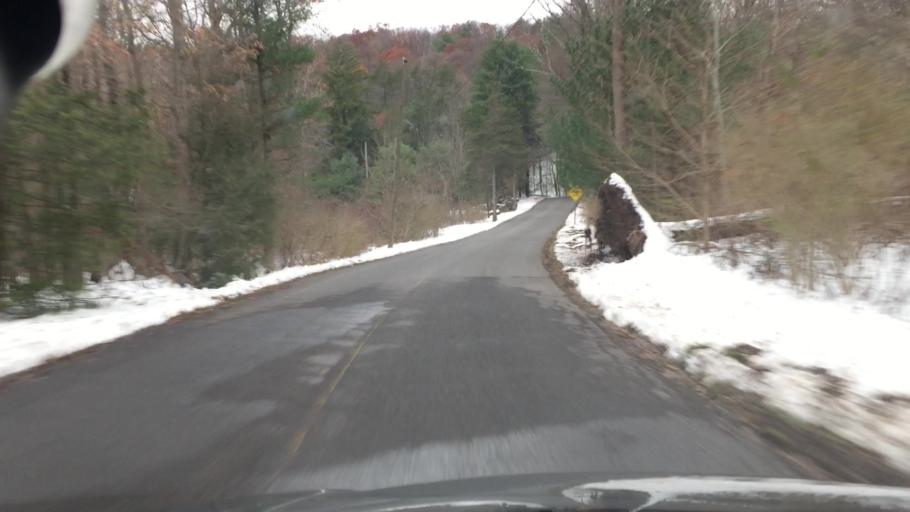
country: US
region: Pennsylvania
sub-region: Luzerne County
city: Conyngham
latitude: 41.0091
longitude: -76.1255
